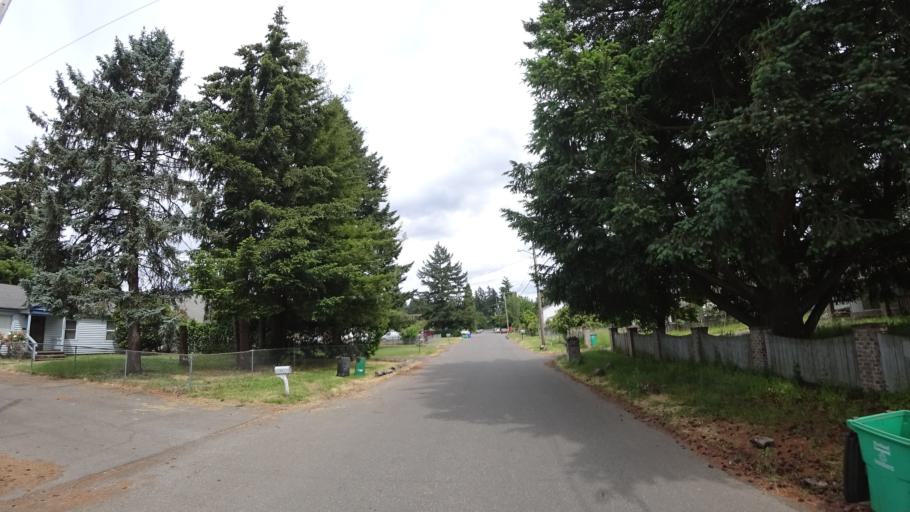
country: US
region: Oregon
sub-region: Multnomah County
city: Lents
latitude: 45.4884
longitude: -122.5409
